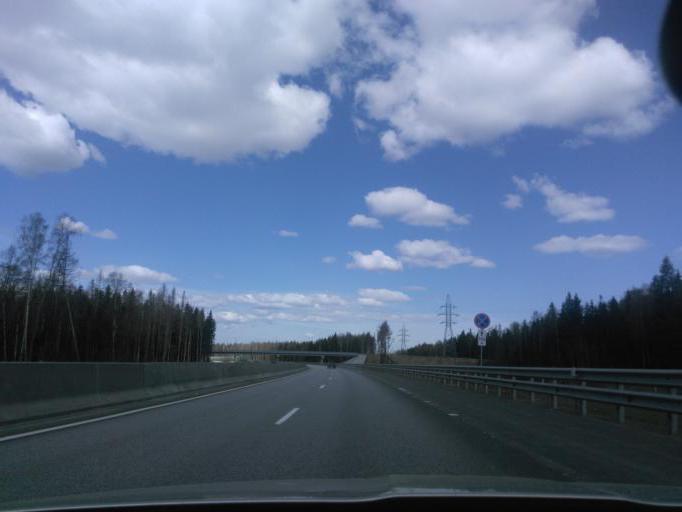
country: RU
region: Moskovskaya
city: Peshki
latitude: 56.1370
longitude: 37.1000
